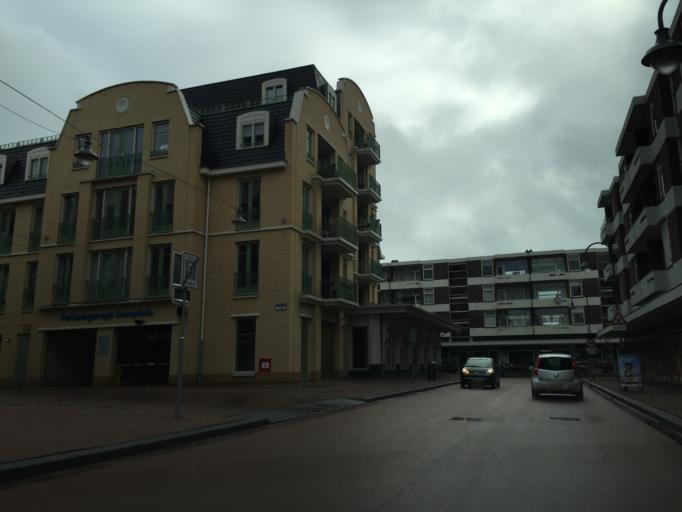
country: NL
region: South Holland
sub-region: Gemeente Leidschendam-Voorburg
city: Voorburg
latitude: 52.0813
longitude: 4.3972
